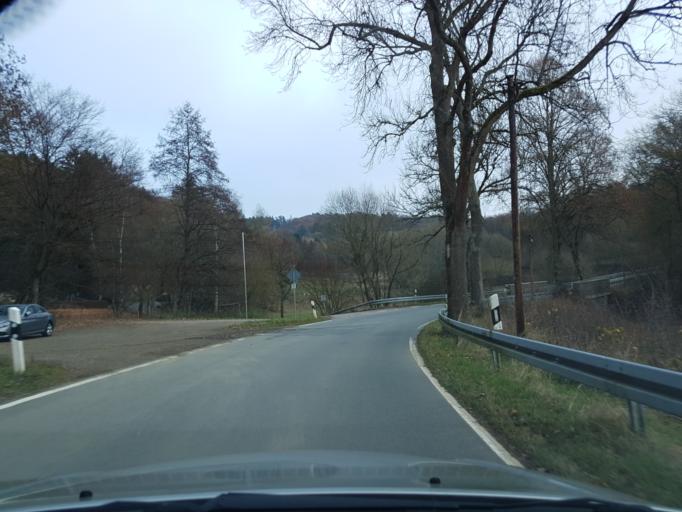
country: DE
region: Hesse
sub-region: Regierungsbezirk Darmstadt
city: Bad Schwalbach
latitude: 50.1387
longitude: 8.0298
